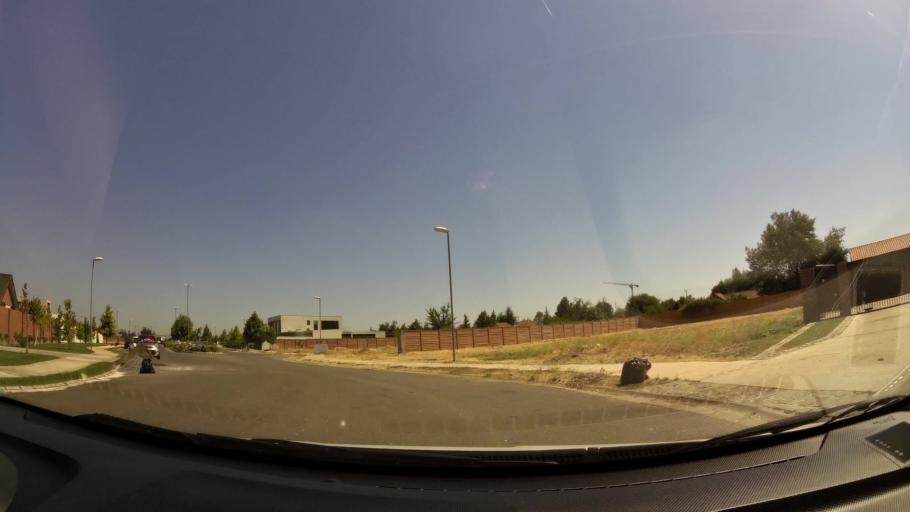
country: CL
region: Maule
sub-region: Provincia de Talca
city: Talca
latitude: -35.4294
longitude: -71.6000
